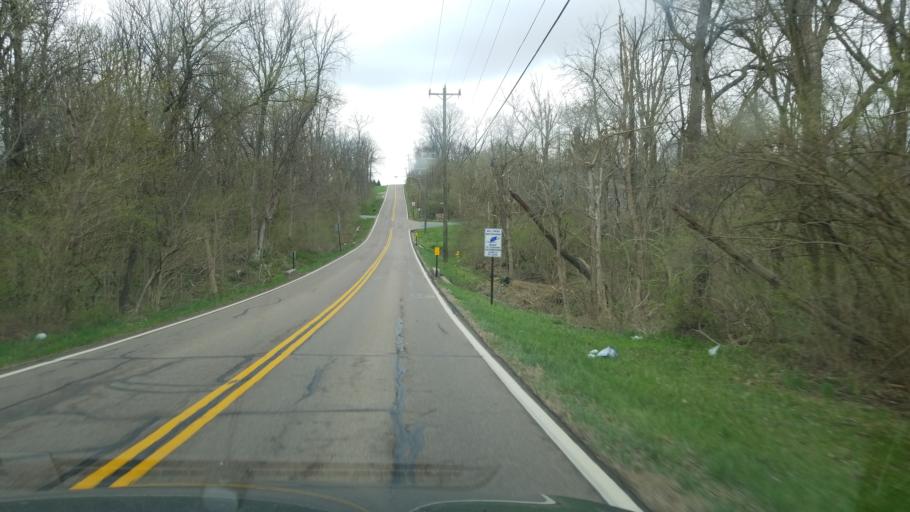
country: US
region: Ohio
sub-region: Butler County
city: Beckett Ridge
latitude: 39.3729
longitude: -84.4402
